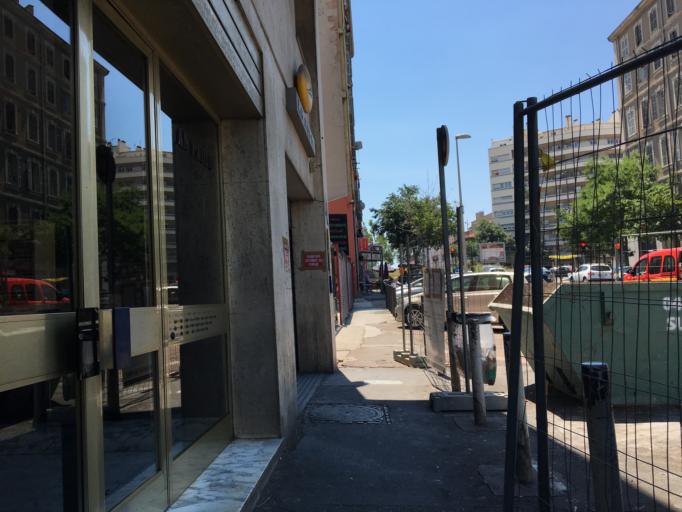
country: FR
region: Provence-Alpes-Cote d'Azur
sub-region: Departement des Bouches-du-Rhone
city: Marseille 03
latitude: 43.3058
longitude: 5.3724
